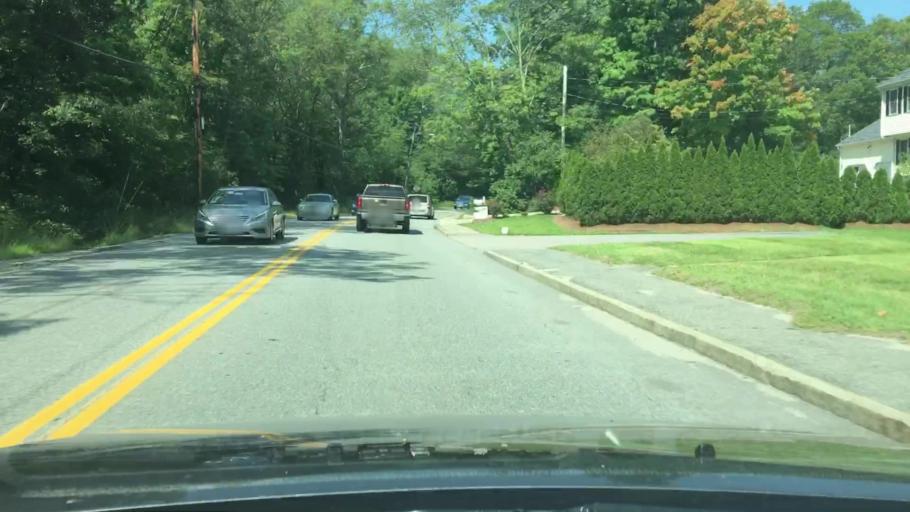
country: US
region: Massachusetts
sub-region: Worcester County
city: Milford
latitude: 42.1579
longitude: -71.5183
